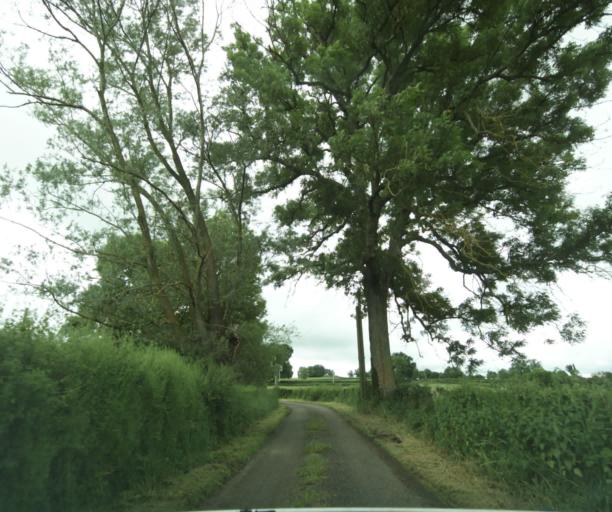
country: FR
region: Bourgogne
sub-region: Departement de Saone-et-Loire
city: Charolles
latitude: 46.4442
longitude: 4.2856
